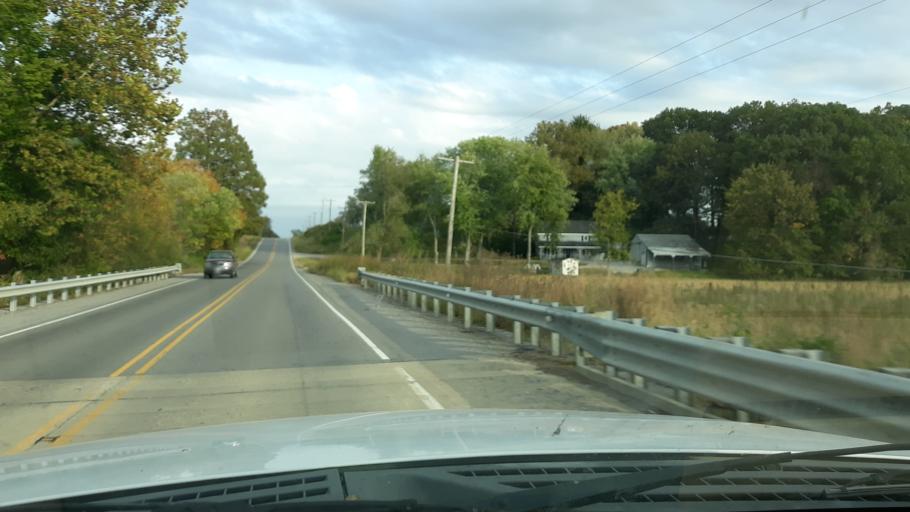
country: US
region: Illinois
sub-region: Saline County
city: Eldorado
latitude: 37.8221
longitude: -88.4950
